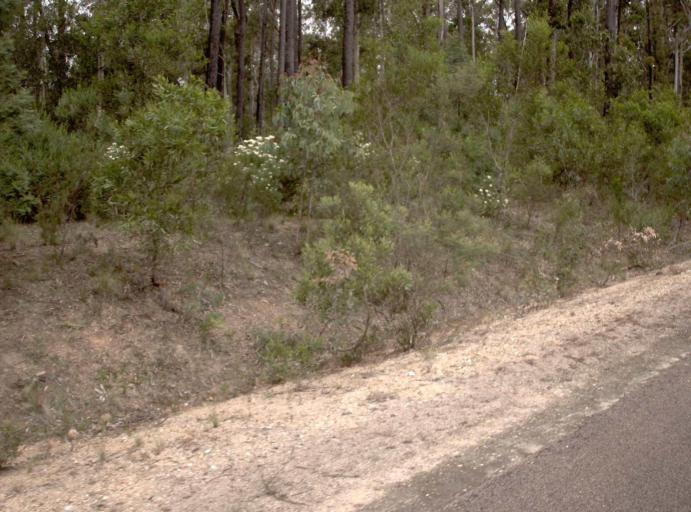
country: AU
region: Victoria
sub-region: East Gippsland
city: Lakes Entrance
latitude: -37.7102
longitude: 148.0715
